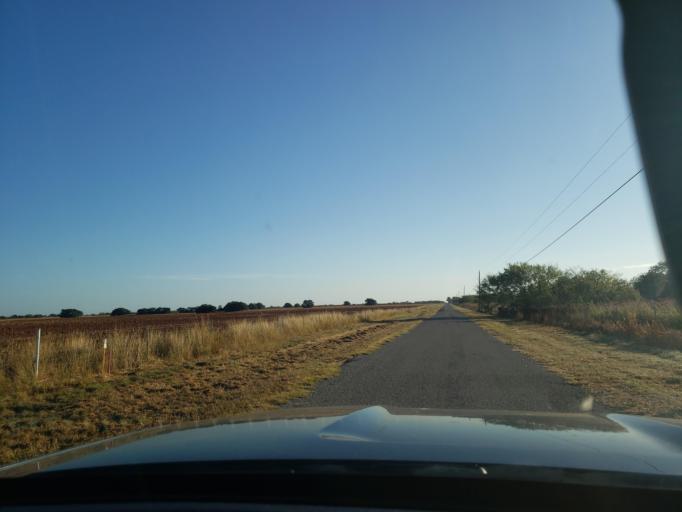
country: US
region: Texas
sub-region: Bee County
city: Beeville
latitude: 28.4267
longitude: -97.6988
